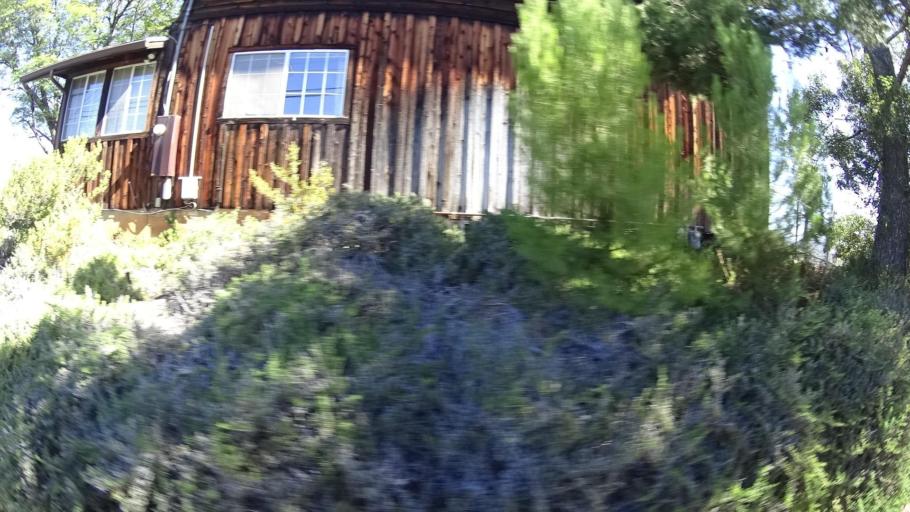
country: US
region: California
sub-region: San Diego County
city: Winter Gardens
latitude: 32.8395
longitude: -116.9421
